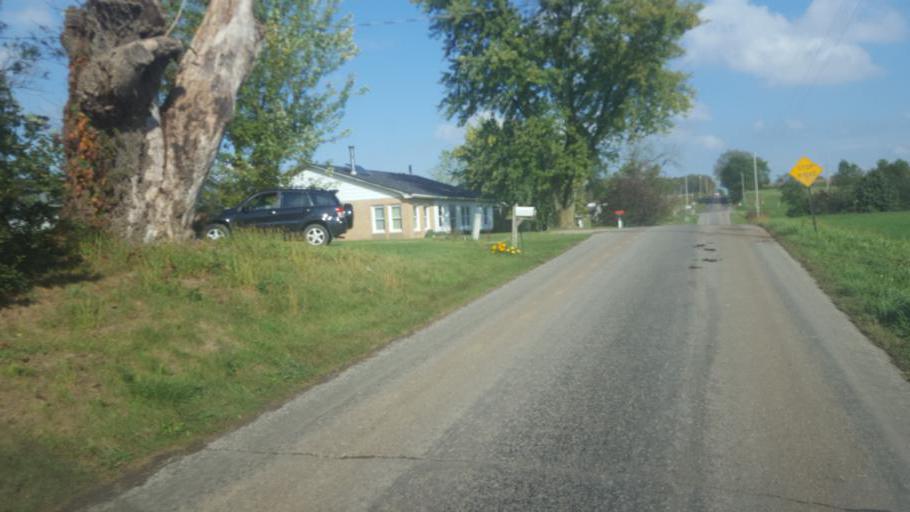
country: US
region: Ohio
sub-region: Wayne County
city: Apple Creek
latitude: 40.6455
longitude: -81.8538
